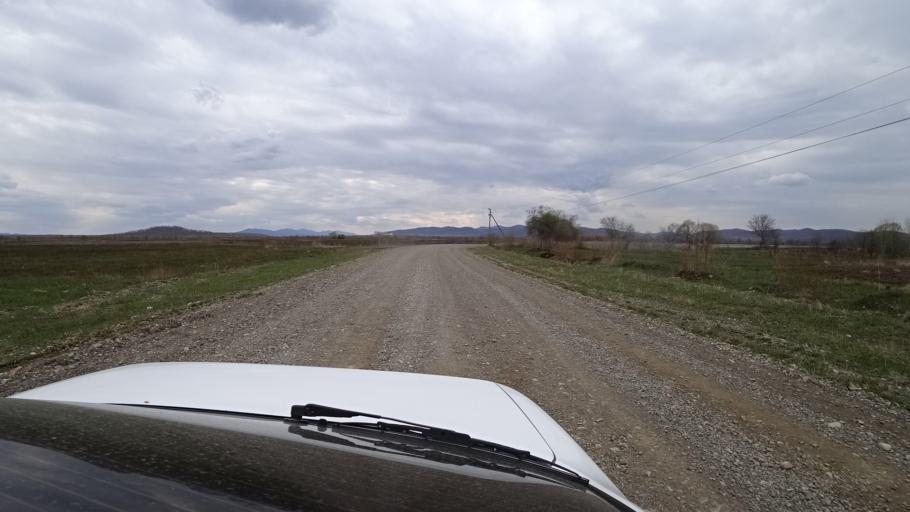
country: RU
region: Primorskiy
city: Novopokrovka
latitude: 45.5772
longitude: 134.3108
